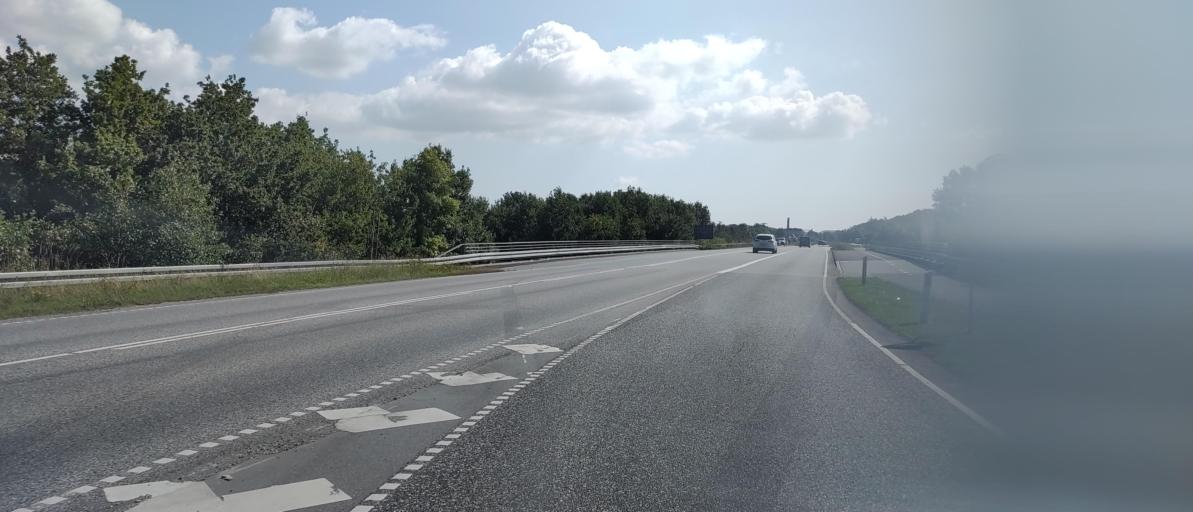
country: DK
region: Zealand
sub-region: Guldborgsund Kommune
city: Norre Alslev
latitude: 54.8631
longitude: 11.8526
